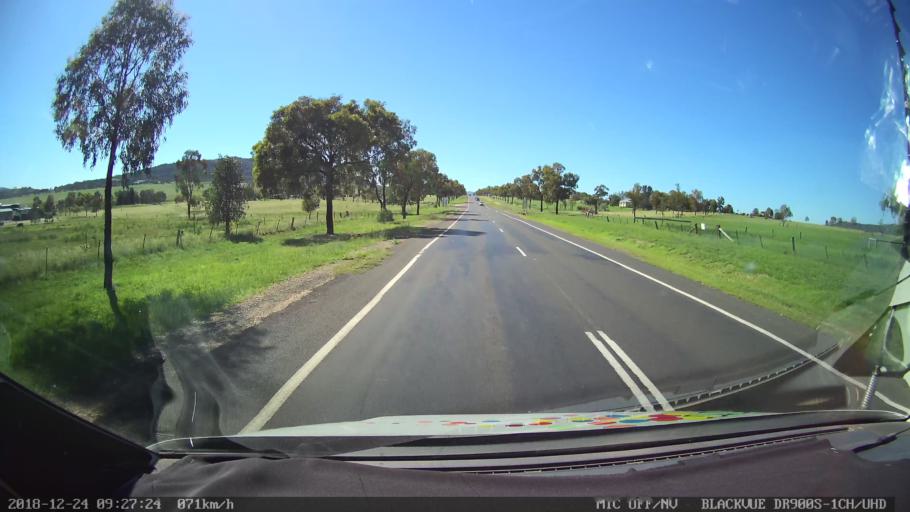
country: AU
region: New South Wales
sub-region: Liverpool Plains
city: Quirindi
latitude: -31.5277
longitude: 150.6808
